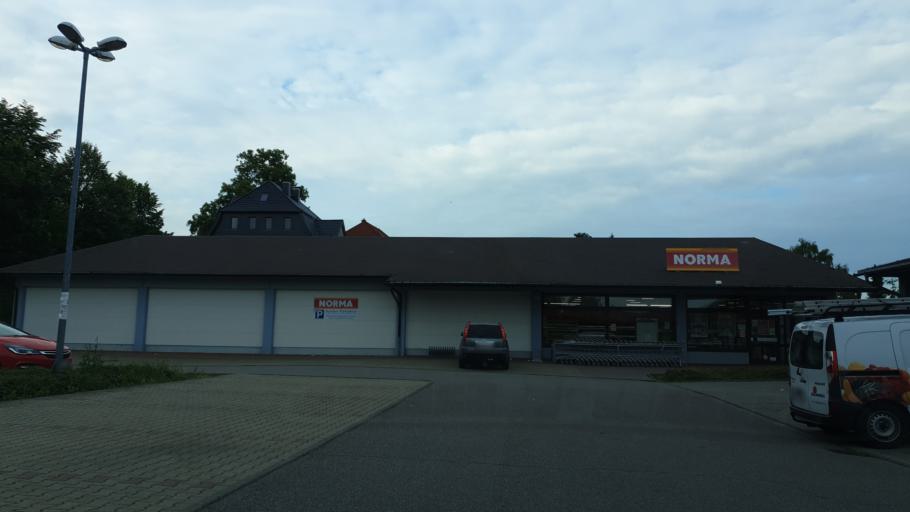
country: DE
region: Saxony
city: Hohenstein-Ernstthal
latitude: 50.8070
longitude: 12.7497
